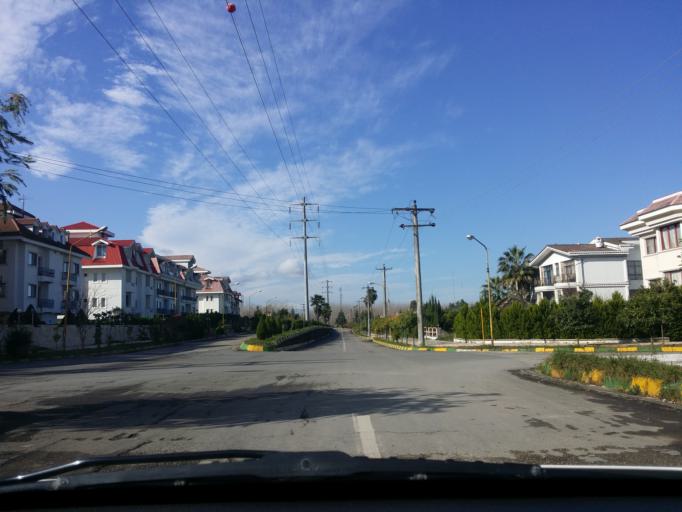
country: IR
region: Mazandaran
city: Chalus
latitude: 36.6746
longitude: 51.3115
